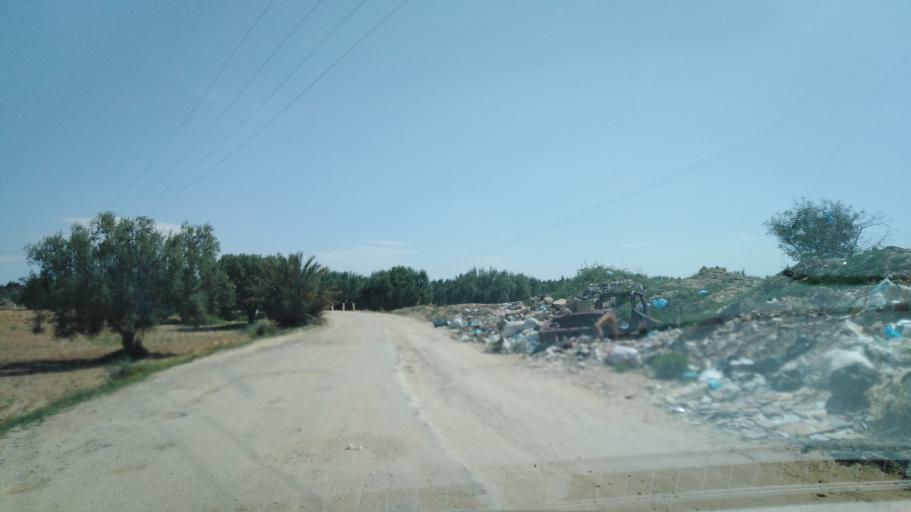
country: TN
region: Safaqis
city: Sfax
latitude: 34.7510
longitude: 10.5268
